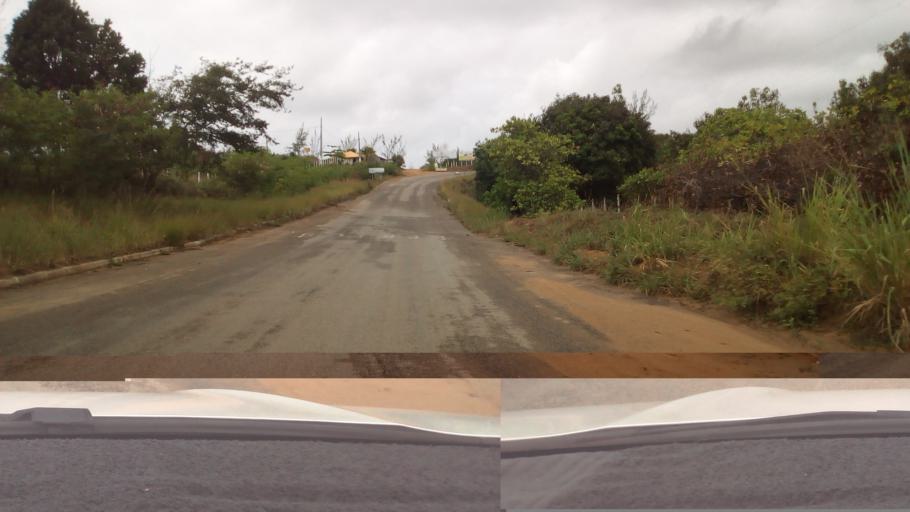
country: BR
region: Paraiba
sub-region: Pitimbu
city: Pitimbu
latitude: -7.4019
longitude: -34.8112
